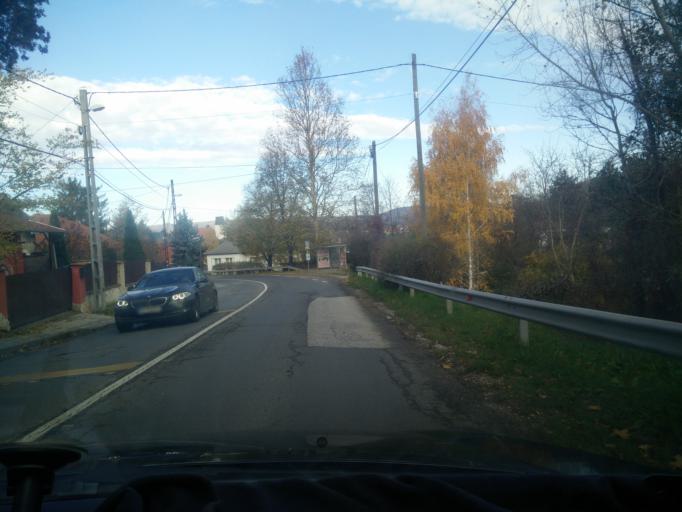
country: HU
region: Pest
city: Solymar
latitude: 47.5876
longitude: 18.9371
